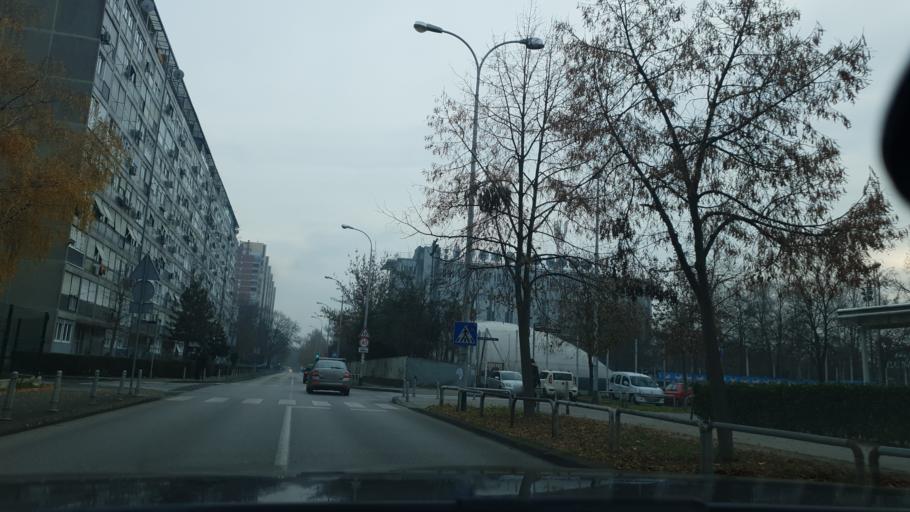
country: HR
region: Grad Zagreb
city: Novi Zagreb
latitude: 45.7750
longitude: 15.9939
